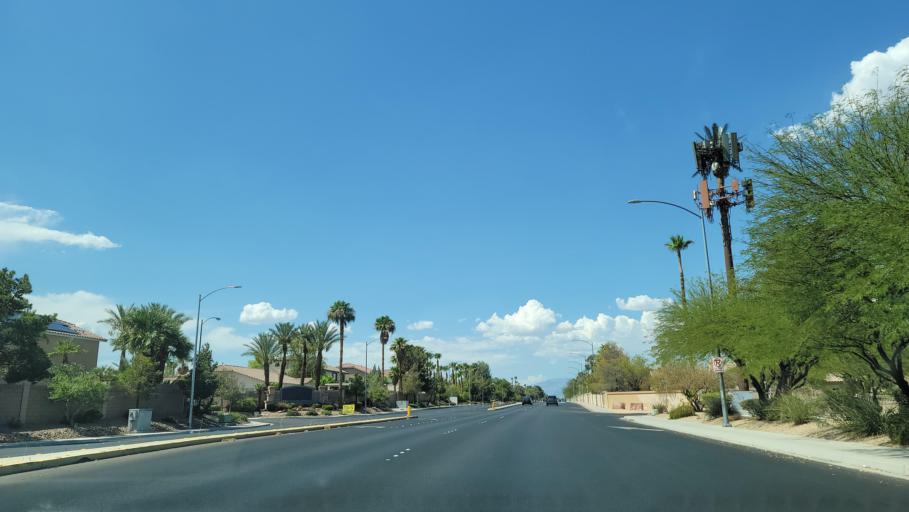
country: US
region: Nevada
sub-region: Clark County
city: Spring Valley
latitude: 36.1303
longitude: -115.2609
